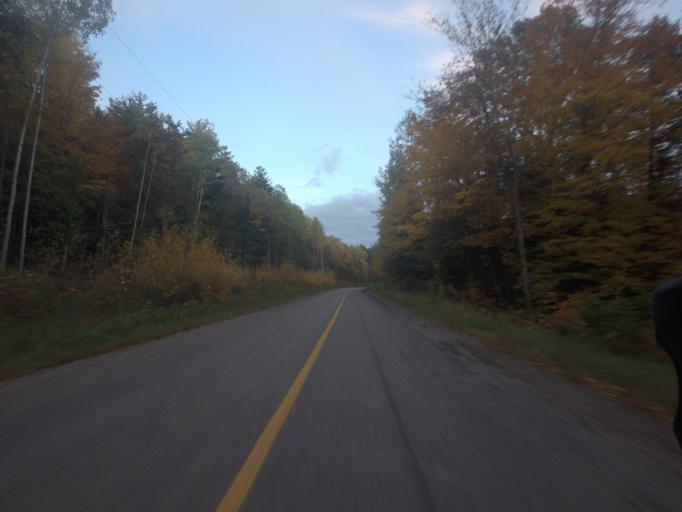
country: CA
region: Ontario
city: Renfrew
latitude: 45.3552
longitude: -76.9560
